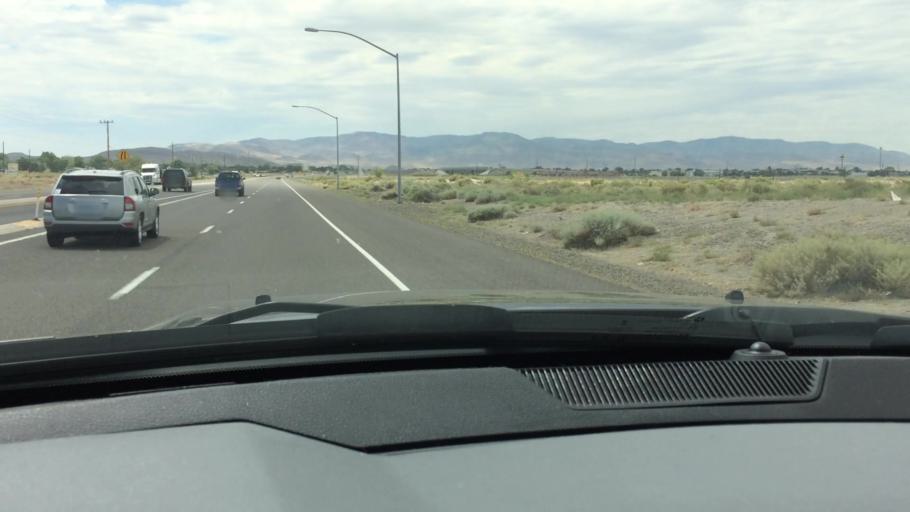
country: US
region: Nevada
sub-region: Lyon County
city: Fernley
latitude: 39.6004
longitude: -119.2119
